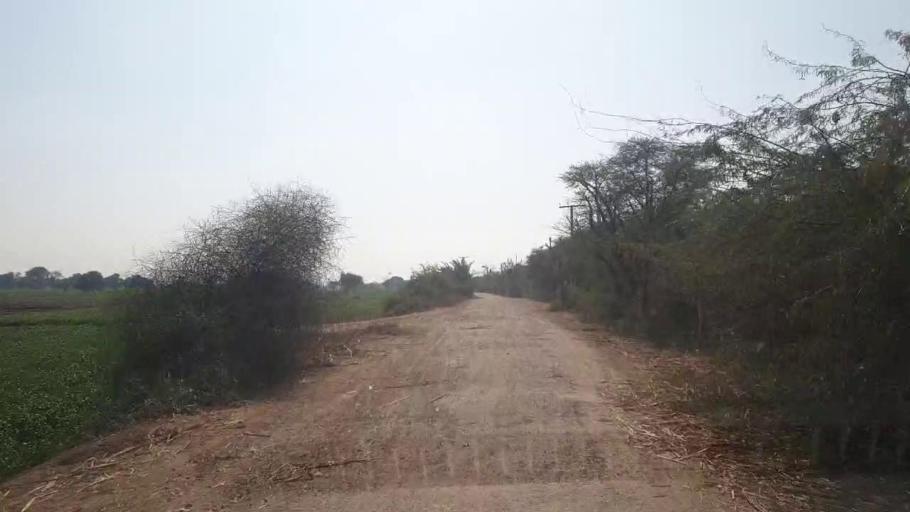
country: PK
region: Sindh
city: Shahdadpur
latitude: 26.0453
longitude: 68.4630
